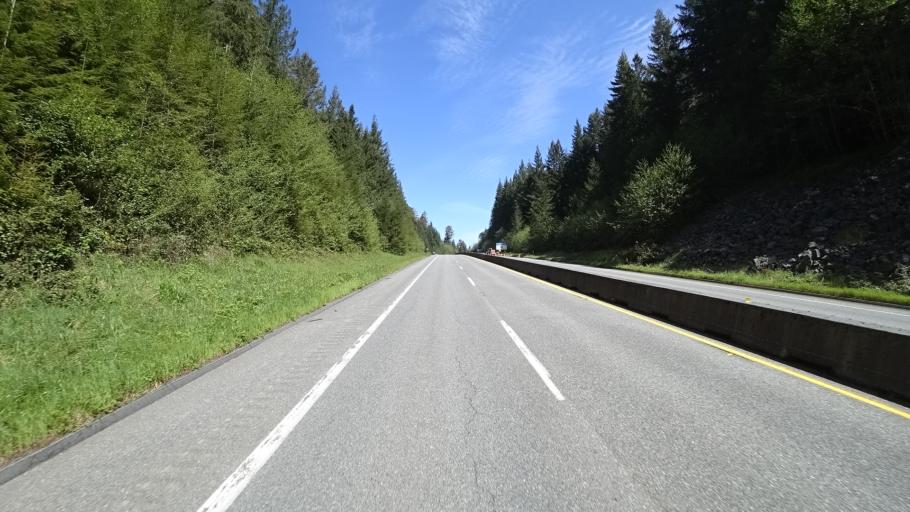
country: US
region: California
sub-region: Humboldt County
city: Westhaven-Moonstone
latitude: 41.3856
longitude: -123.9950
